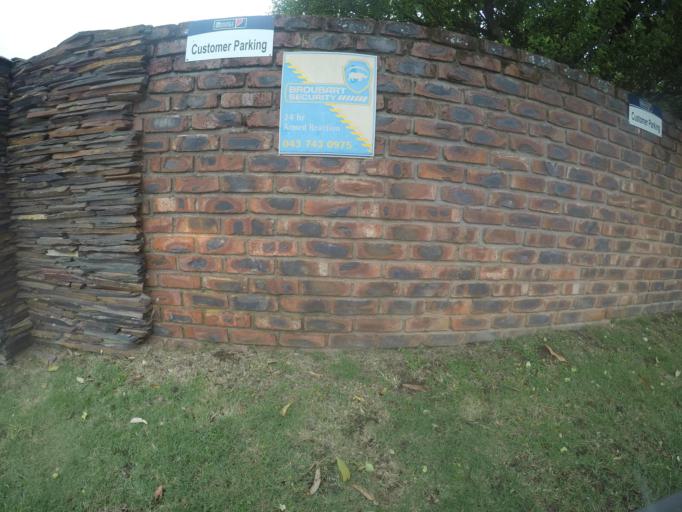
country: ZA
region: Eastern Cape
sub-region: Buffalo City Metropolitan Municipality
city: East London
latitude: -32.9673
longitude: 27.8461
